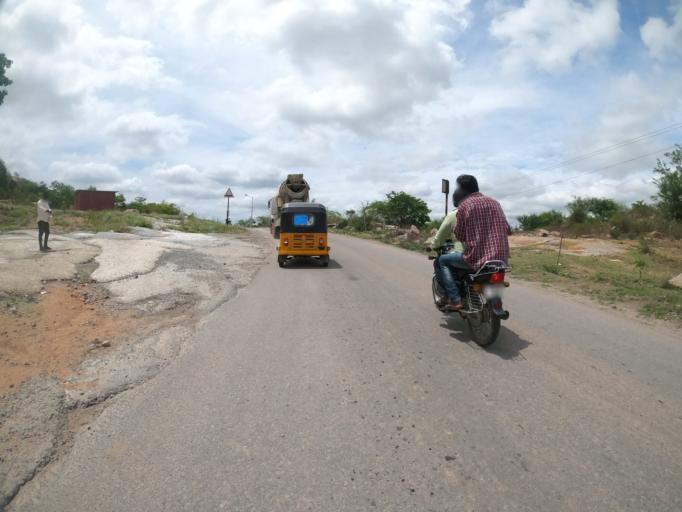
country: IN
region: Telangana
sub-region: Hyderabad
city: Hyderabad
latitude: 17.3132
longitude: 78.3721
